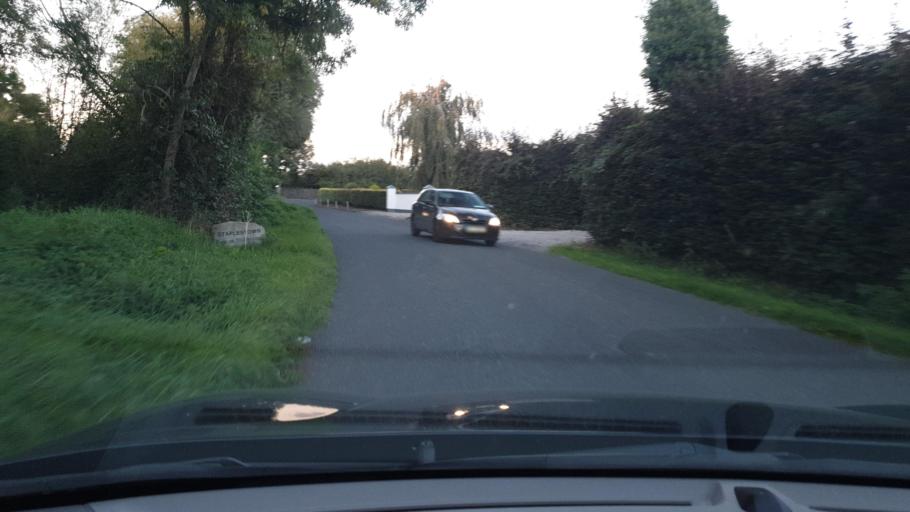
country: IE
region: Leinster
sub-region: Kildare
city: Prosperous
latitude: 53.3272
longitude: -6.7811
